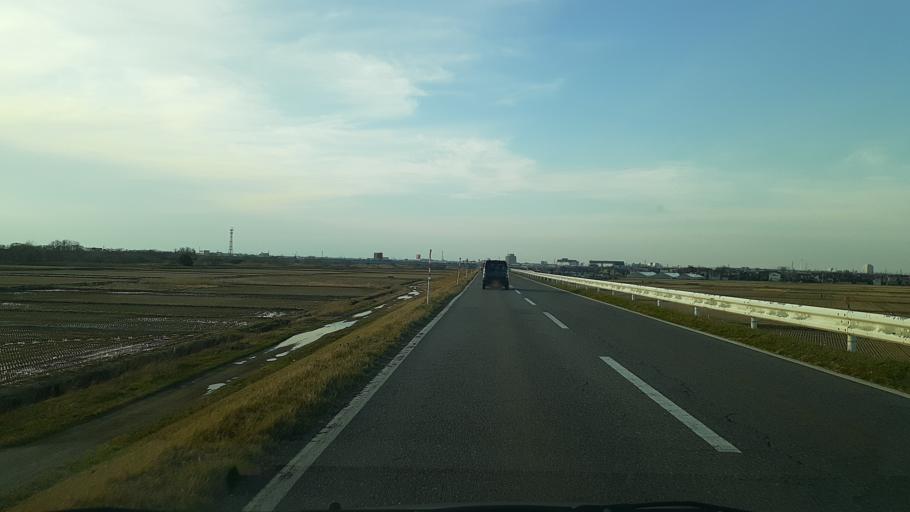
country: JP
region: Niigata
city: Niigata-shi
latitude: 37.8476
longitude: 139.0292
